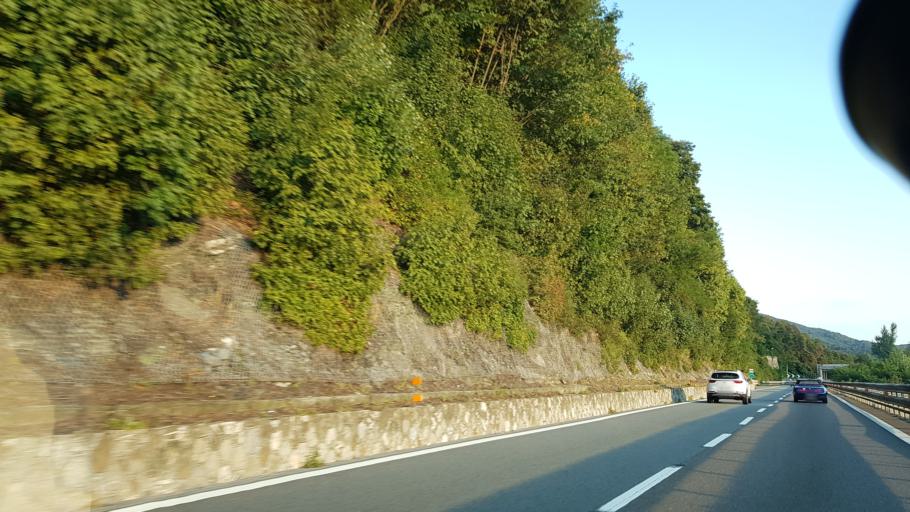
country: IT
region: Liguria
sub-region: Provincia di Genova
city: Borgo Fornari-Pieve
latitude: 44.5873
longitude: 8.9411
